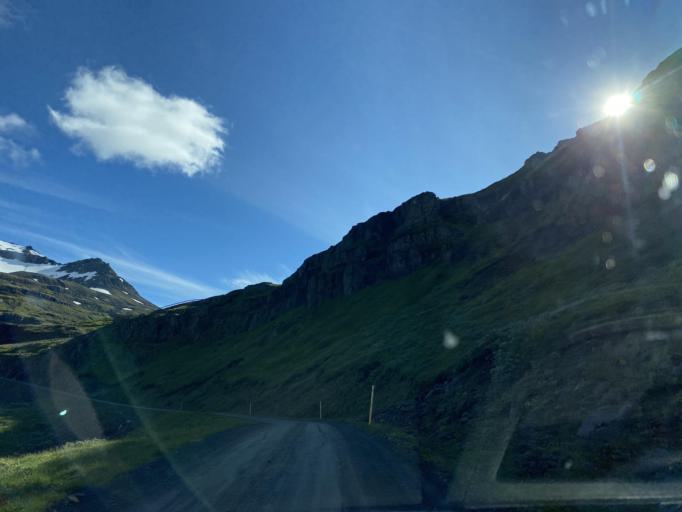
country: IS
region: East
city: Eskifjoerdur
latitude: 65.1825
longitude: -14.0843
